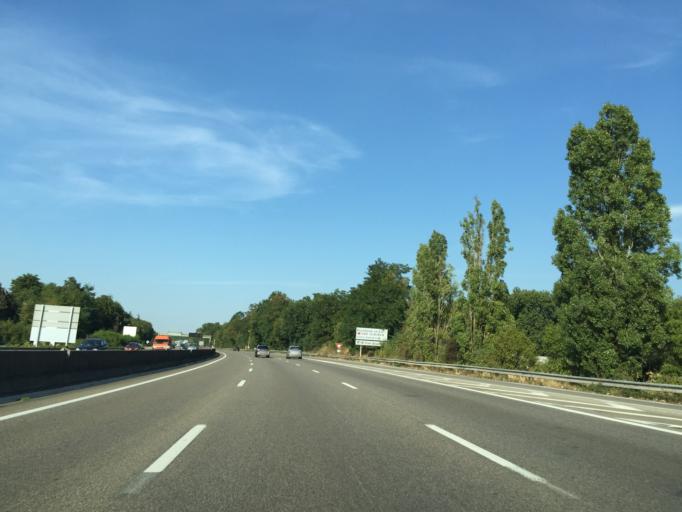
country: FR
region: Alsace
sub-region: Departement du Bas-Rhin
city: Ostwald
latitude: 48.5381
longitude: 7.7176
